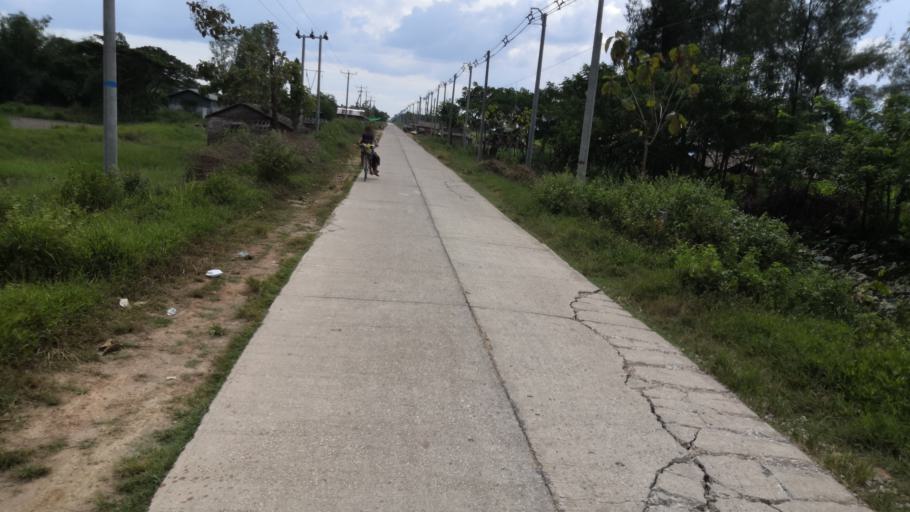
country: MM
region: Yangon
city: Kanbe
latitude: 16.4703
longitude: 96.1445
